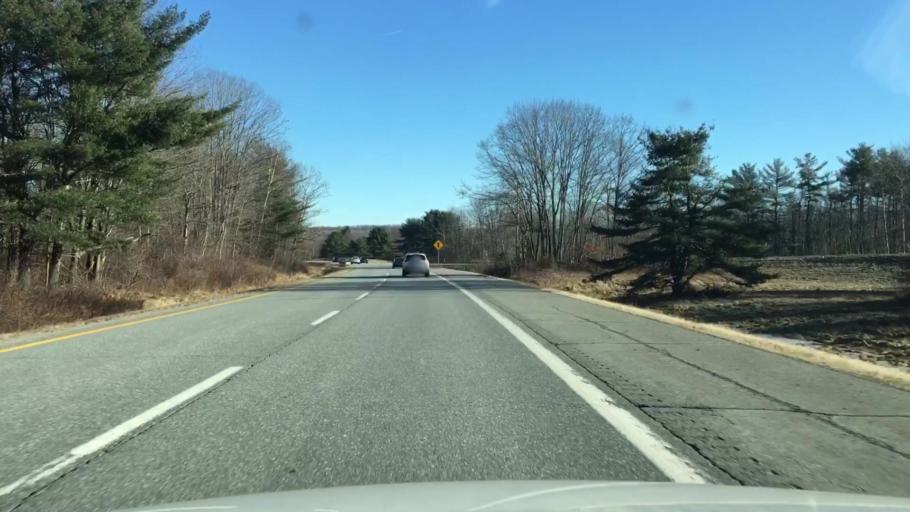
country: US
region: Maine
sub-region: Penobscot County
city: Hermon
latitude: 44.7584
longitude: -68.9738
